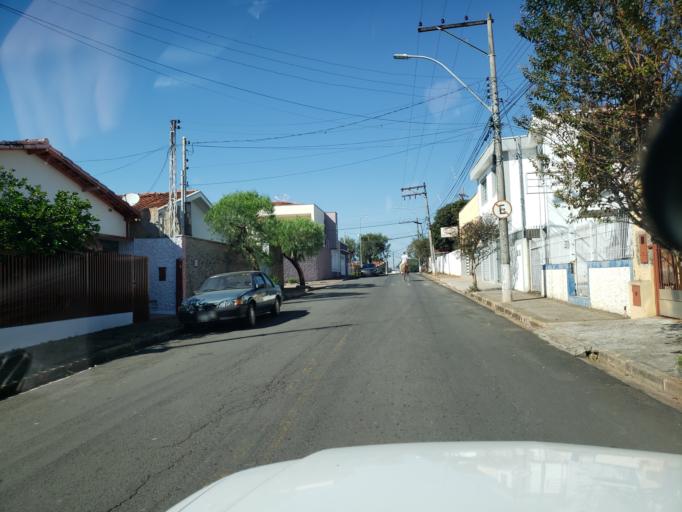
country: BR
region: Sao Paulo
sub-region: Itapira
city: Itapira
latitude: -22.4380
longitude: -46.8322
